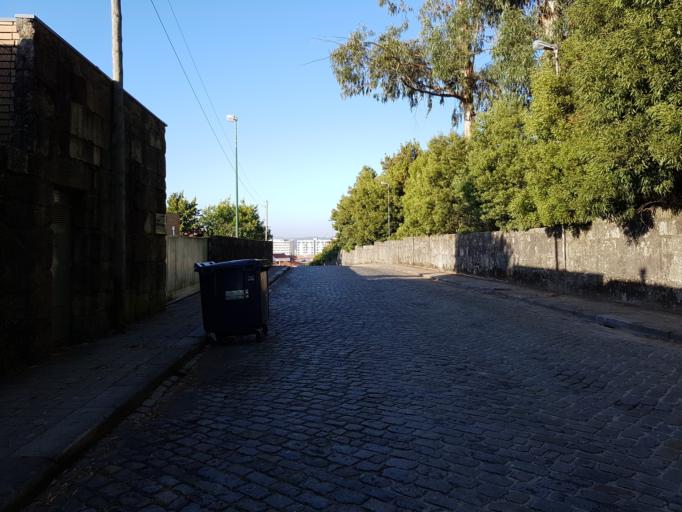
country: PT
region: Porto
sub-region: Porto
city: Porto
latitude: 41.1604
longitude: -8.5887
